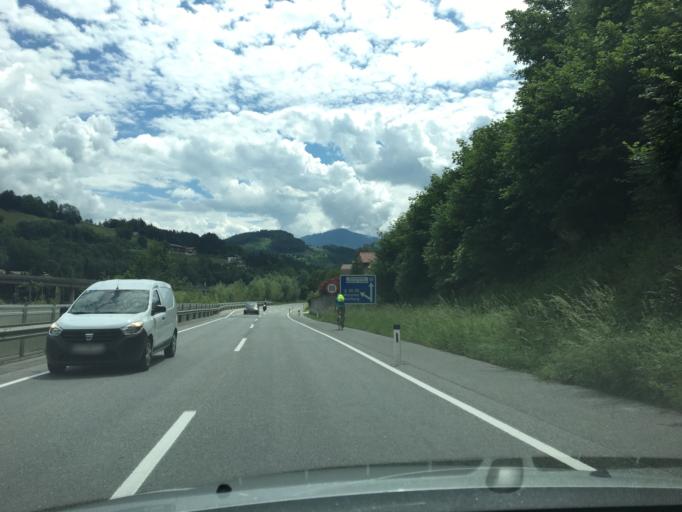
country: AT
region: Salzburg
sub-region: Politischer Bezirk Sankt Johann im Pongau
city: Werfen
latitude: 47.4684
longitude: 13.1953
